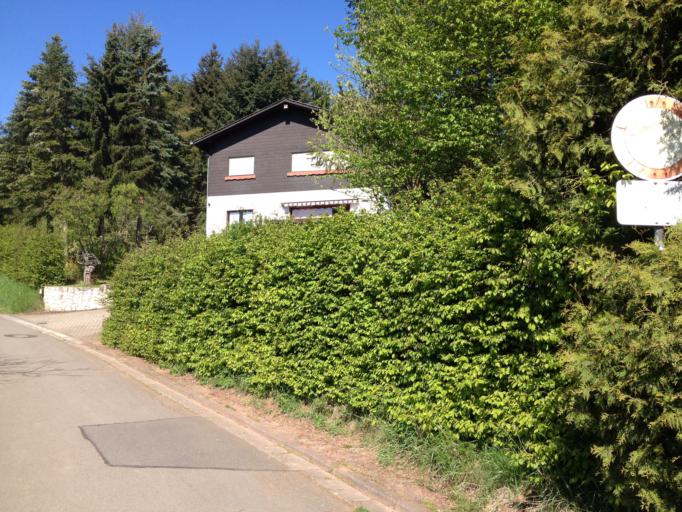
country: DE
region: Saarland
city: Hangard
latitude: 49.3837
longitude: 7.2053
